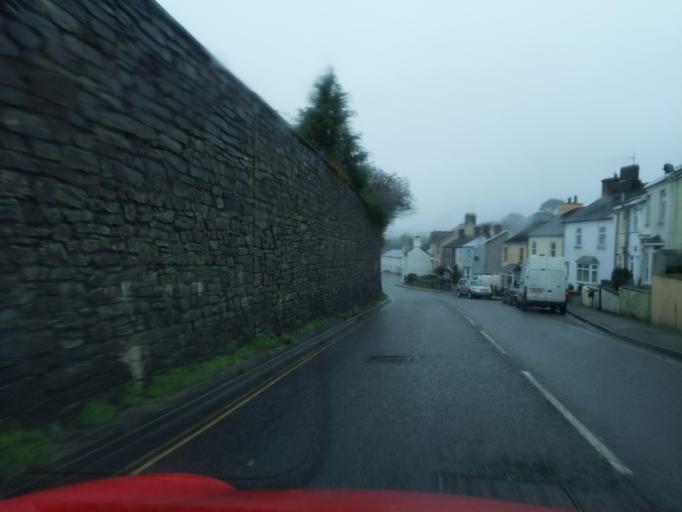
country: GB
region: England
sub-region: Cornwall
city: Callington
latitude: 50.5033
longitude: -4.3138
